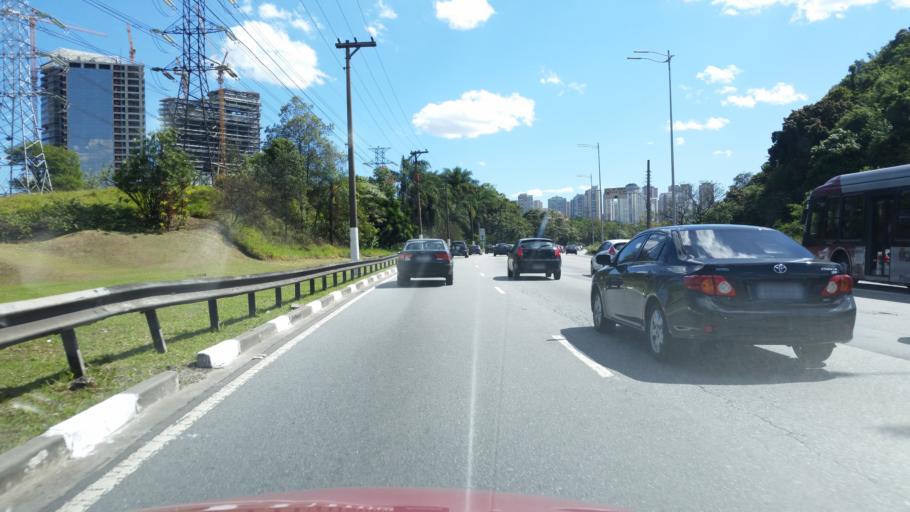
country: BR
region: Sao Paulo
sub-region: Taboao Da Serra
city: Taboao da Serra
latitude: -23.6213
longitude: -46.7036
